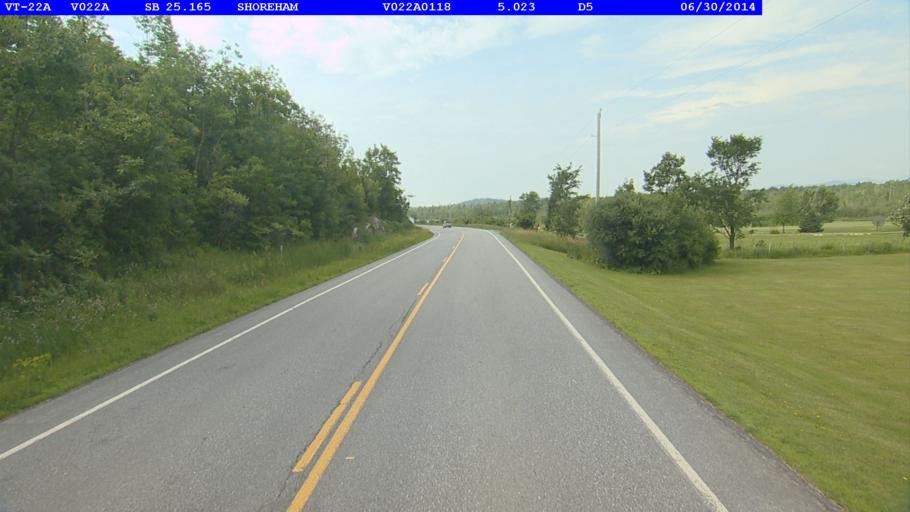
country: US
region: New York
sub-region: Essex County
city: Ticonderoga
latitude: 43.9215
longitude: -73.3122
